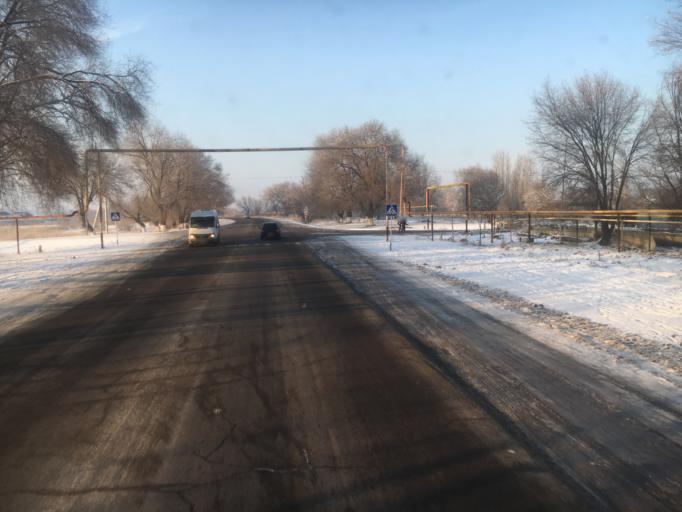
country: KZ
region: Almaty Oblysy
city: Burunday
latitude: 43.3391
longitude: 76.6591
